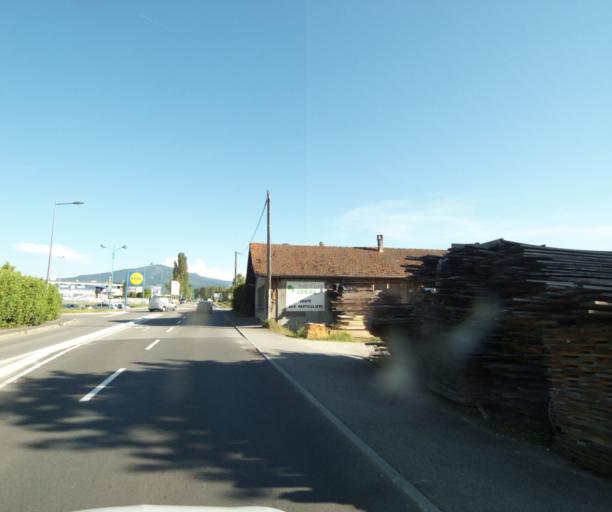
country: FR
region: Rhone-Alpes
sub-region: Departement de la Haute-Savoie
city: Douvaine
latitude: 46.2997
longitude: 6.3045
